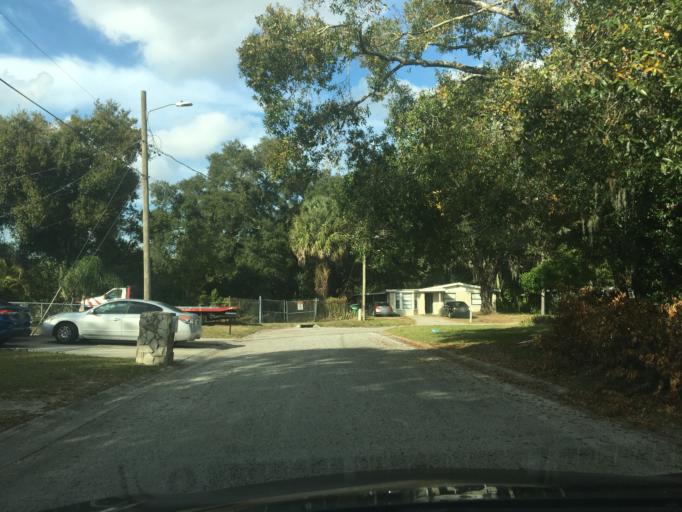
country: US
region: Florida
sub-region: Hillsborough County
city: Temple Terrace
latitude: 28.0264
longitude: -82.4137
